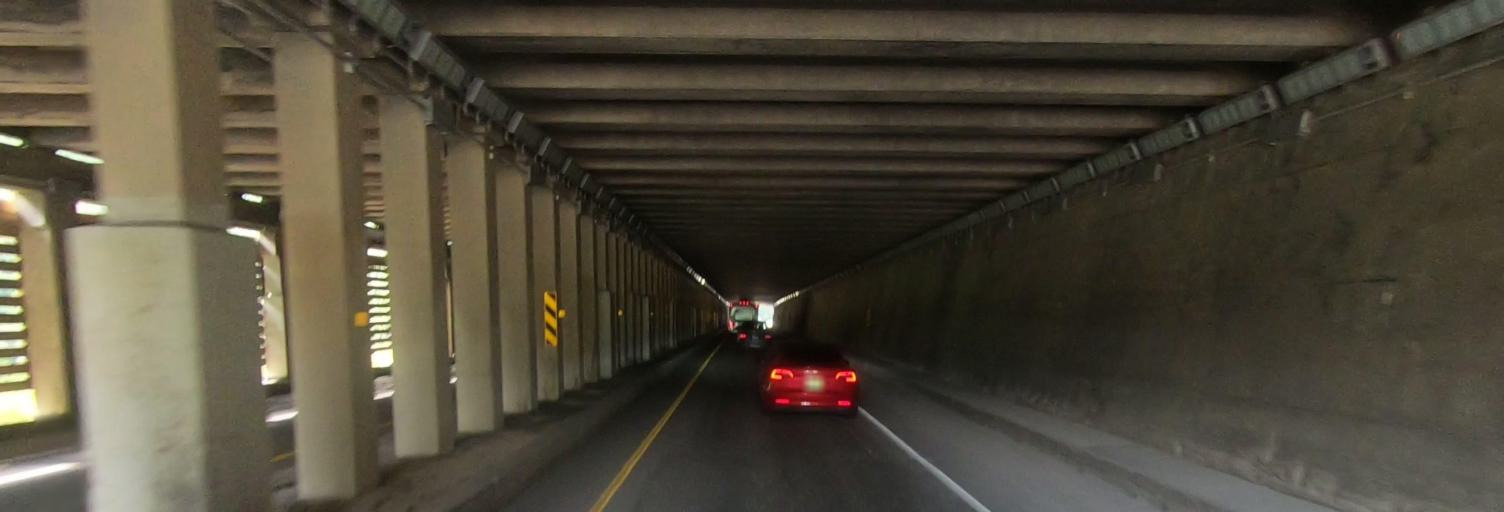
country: CA
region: British Columbia
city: Golden
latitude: 51.3243
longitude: -117.4792
